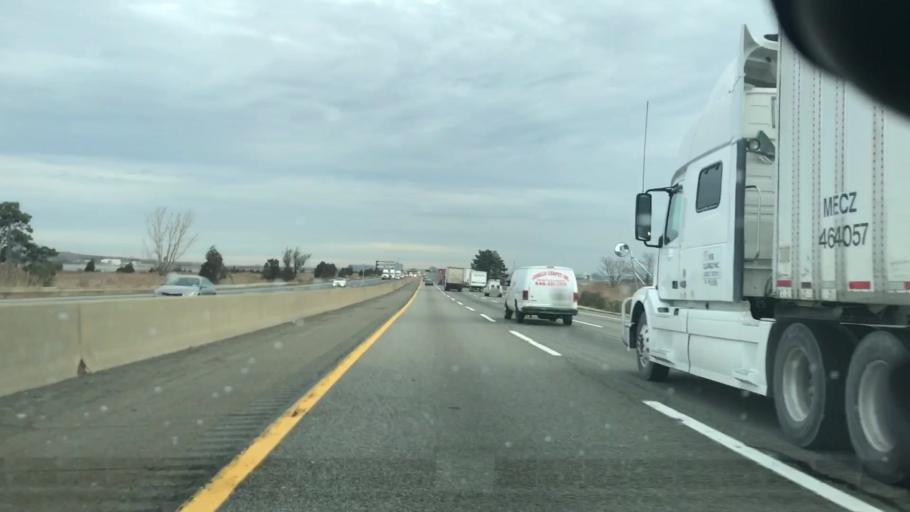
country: US
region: New Jersey
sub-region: Bergen County
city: North Arlington
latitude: 40.7650
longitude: -74.1110
